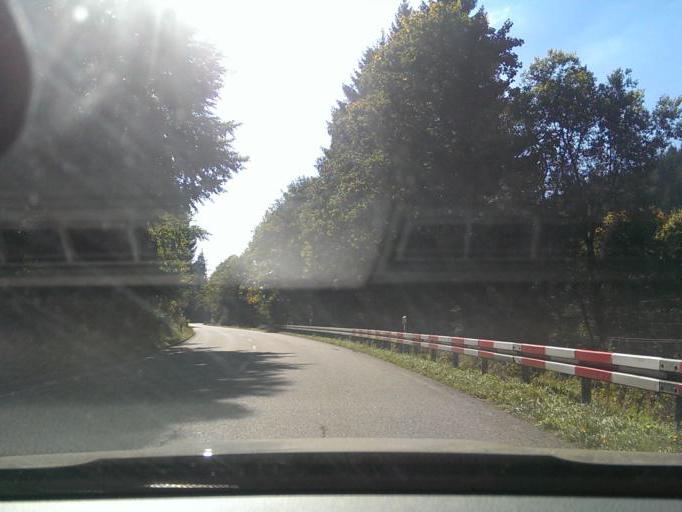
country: DE
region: Baden-Wuerttemberg
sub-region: Karlsruhe Region
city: Bad Herrenalb
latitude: 48.8491
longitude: 8.4384
